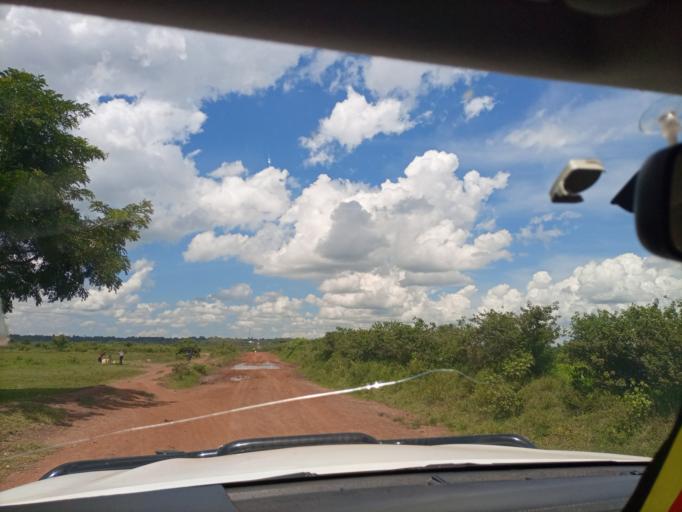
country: UG
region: Eastern Region
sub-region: Busia District
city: Busia
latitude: 0.6296
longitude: 33.9909
